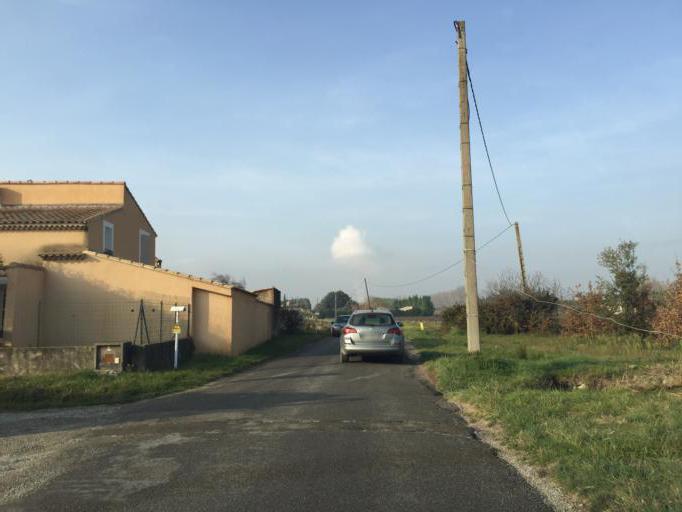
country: FR
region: Provence-Alpes-Cote d'Azur
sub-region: Departement du Vaucluse
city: Jonquieres
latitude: 44.1265
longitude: 4.8804
